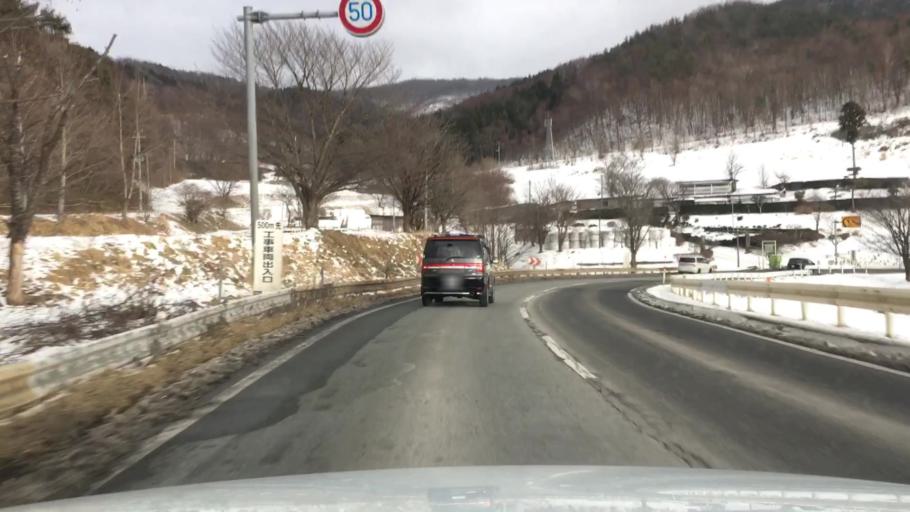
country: JP
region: Iwate
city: Morioka-shi
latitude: 39.6707
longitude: 141.3292
